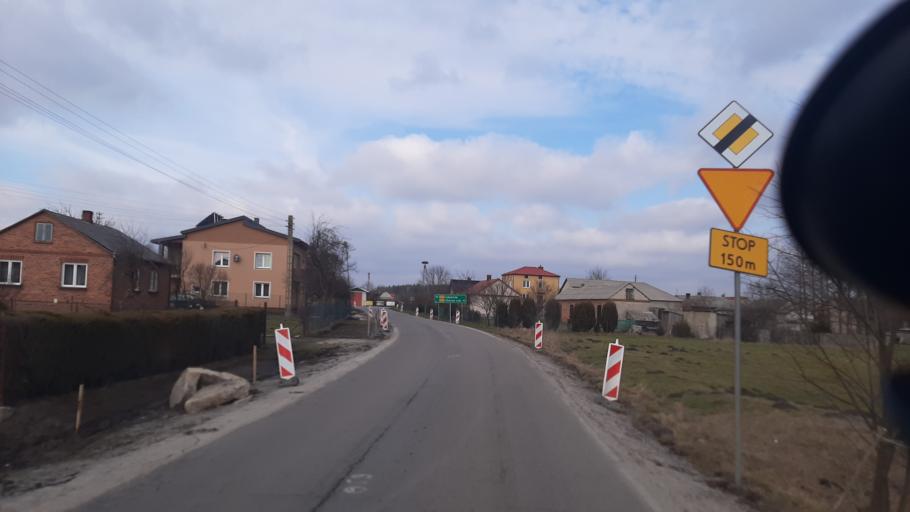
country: PL
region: Lublin Voivodeship
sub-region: Powiat lubartowski
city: Niedzwiada
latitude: 51.4921
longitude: 22.7604
